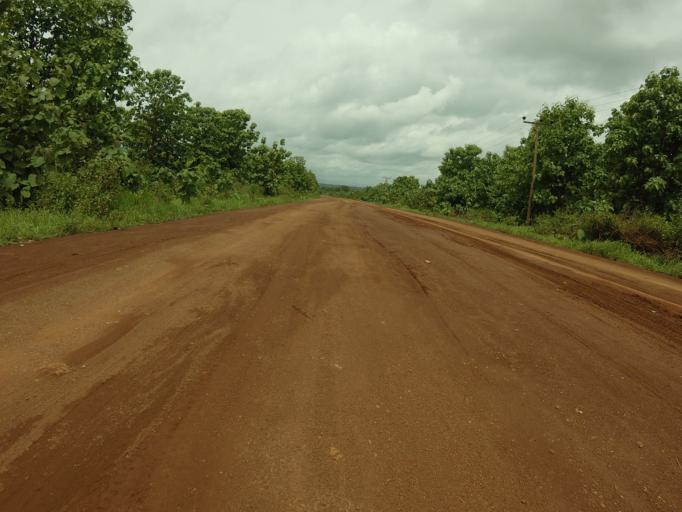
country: GH
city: Kpandae
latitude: 8.4103
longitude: 0.3946
